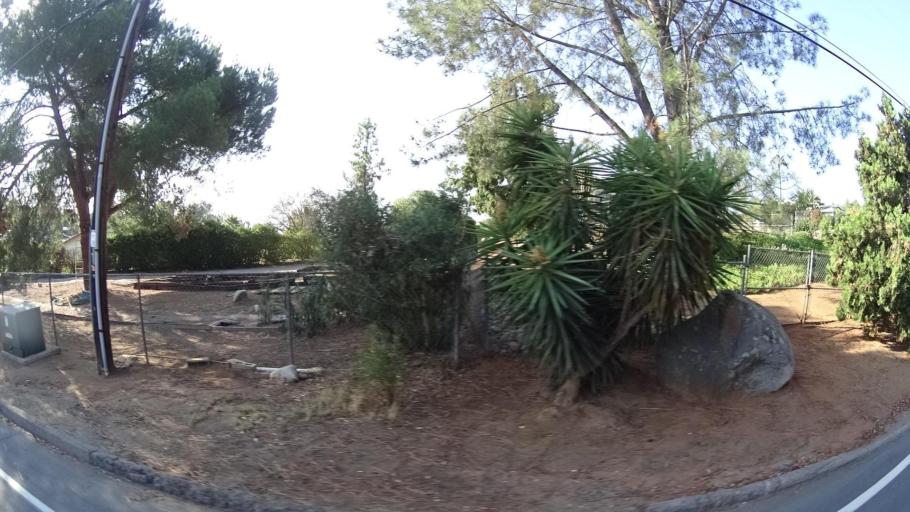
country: US
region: California
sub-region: San Diego County
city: Eucalyptus Hills
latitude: 32.8826
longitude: -116.9433
